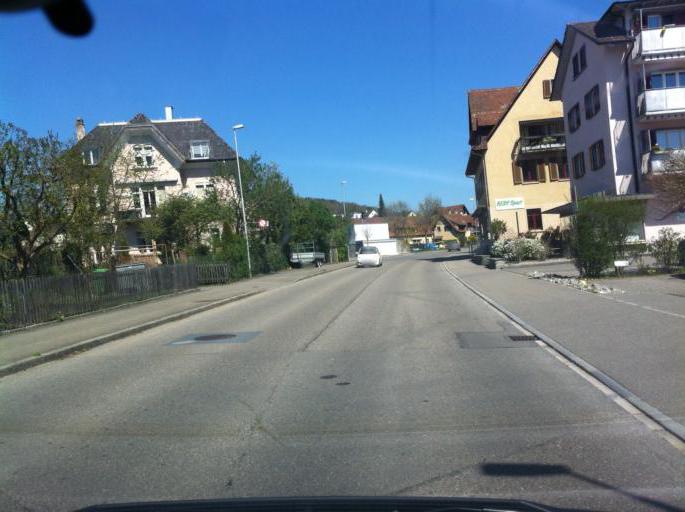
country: CH
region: Schaffhausen
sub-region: Bezirk Schaffhausen
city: Schaffhausen
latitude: 47.7075
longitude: 8.6276
